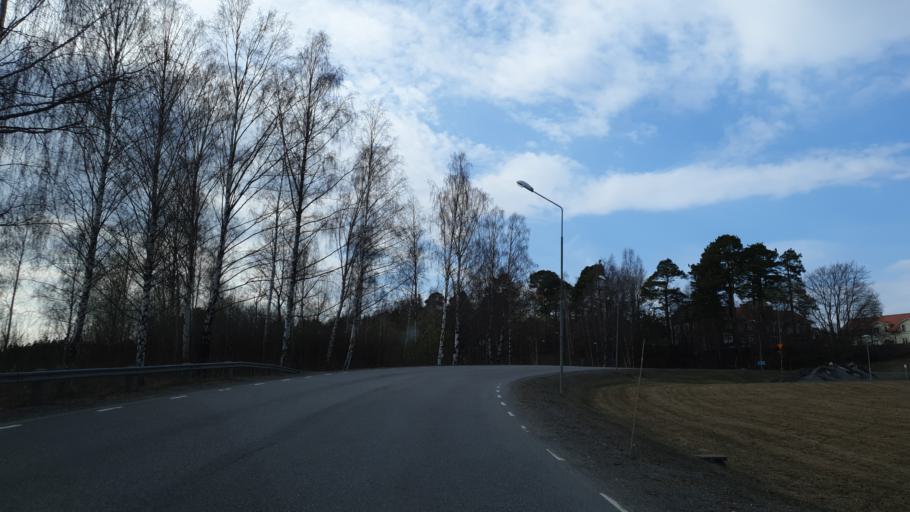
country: SE
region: Gaevleborg
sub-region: Hudiksvalls Kommun
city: Iggesund
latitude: 61.6399
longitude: 17.0746
